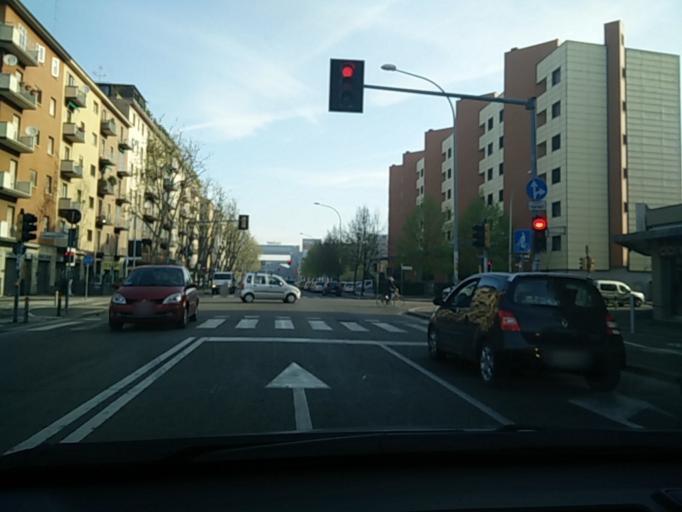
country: IT
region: Emilia-Romagna
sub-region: Provincia di Bologna
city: Bologna
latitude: 44.5074
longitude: 11.3553
